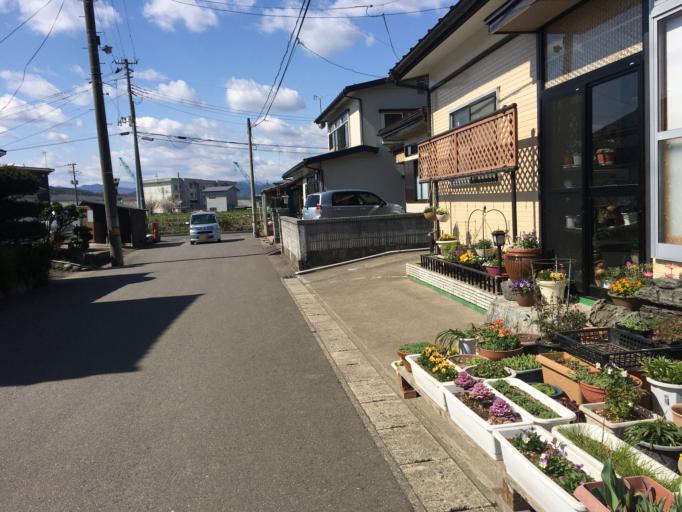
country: JP
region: Aomori
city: Hachinohe
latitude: 40.2016
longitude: 141.7936
